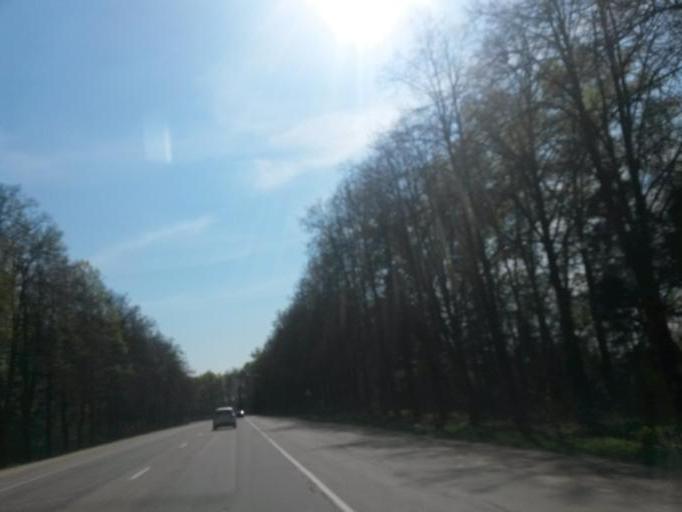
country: RU
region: Moskovskaya
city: Stolbovaya
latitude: 55.2510
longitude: 37.5047
